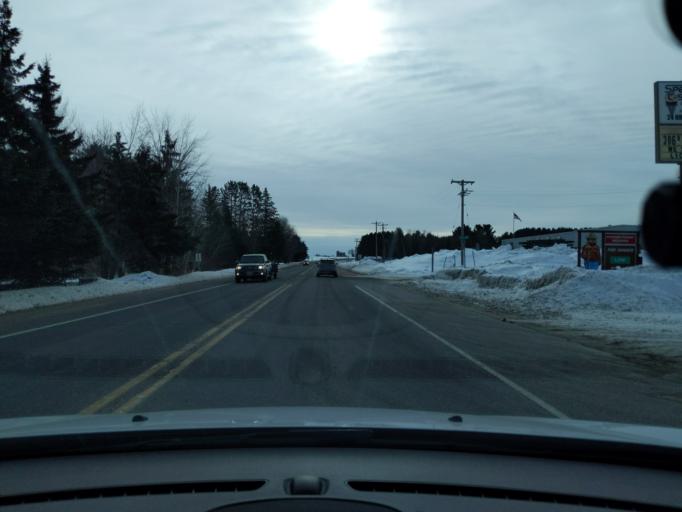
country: US
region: Wisconsin
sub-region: Barron County
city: Cumberland
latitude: 45.6354
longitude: -91.9926
